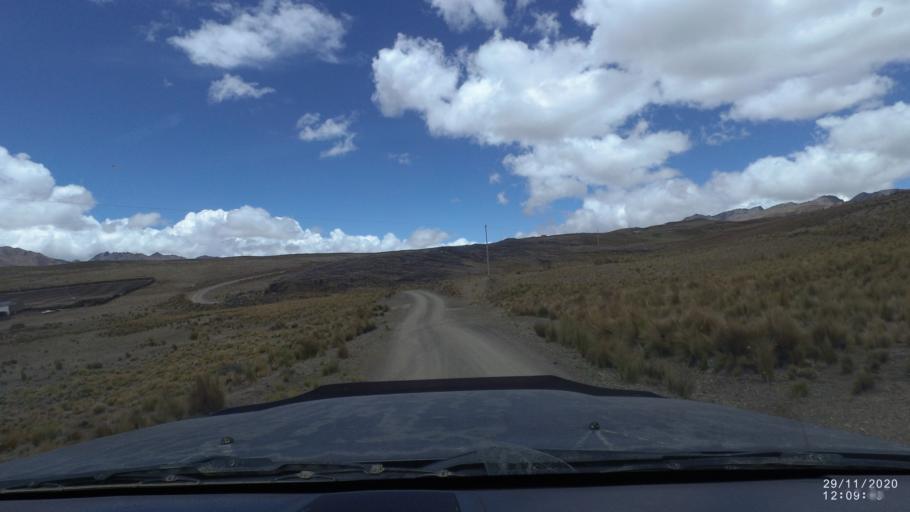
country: BO
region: Cochabamba
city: Cochabamba
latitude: -17.1291
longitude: -66.3048
